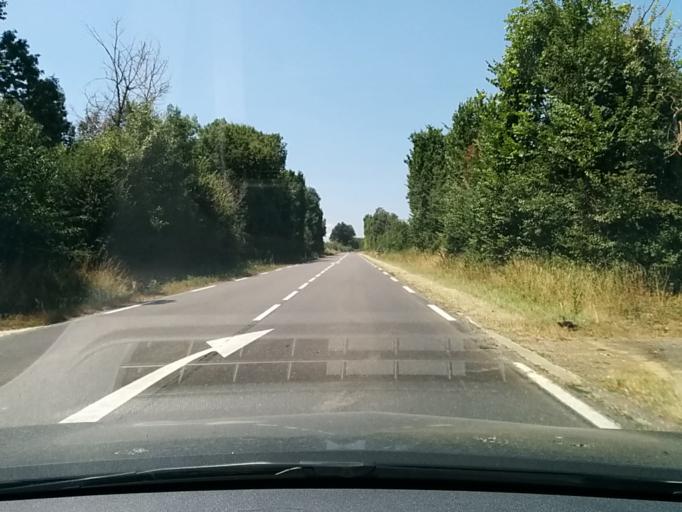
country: FR
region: Midi-Pyrenees
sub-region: Departement du Gers
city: Gimont
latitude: 43.6177
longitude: 0.9206
